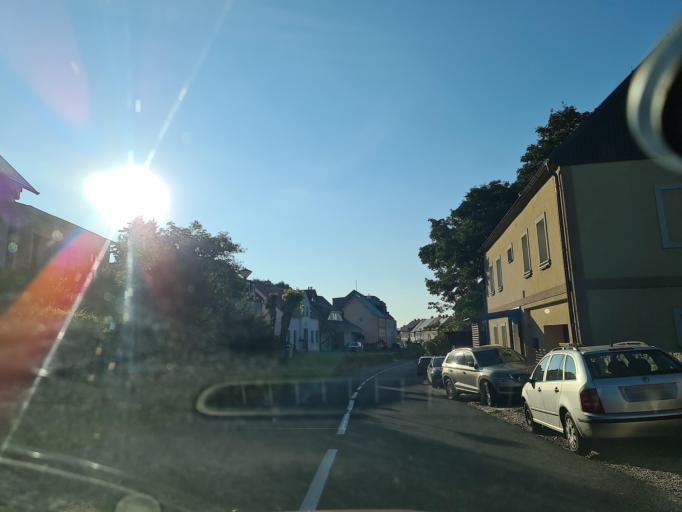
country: DE
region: Saxony
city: Deutschneudorf
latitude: 50.6047
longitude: 13.4428
